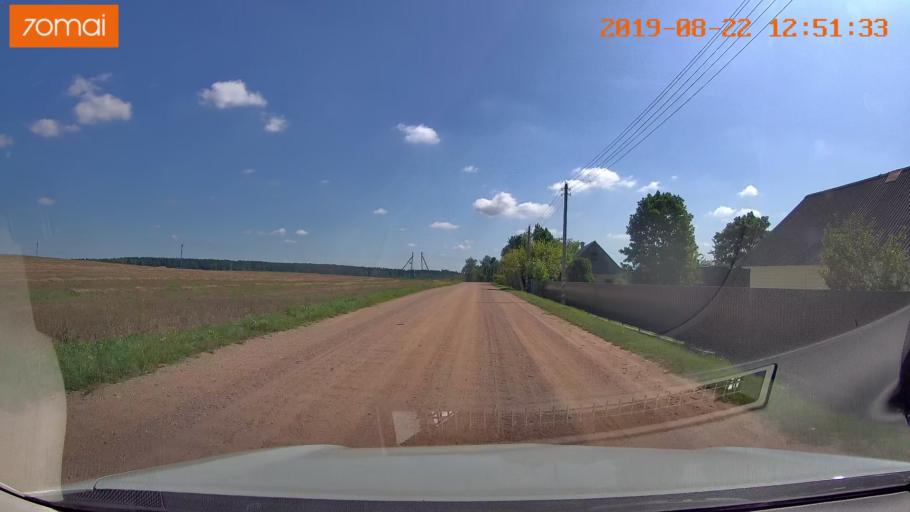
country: BY
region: Minsk
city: Prawdzinski
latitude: 53.4574
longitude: 27.6569
